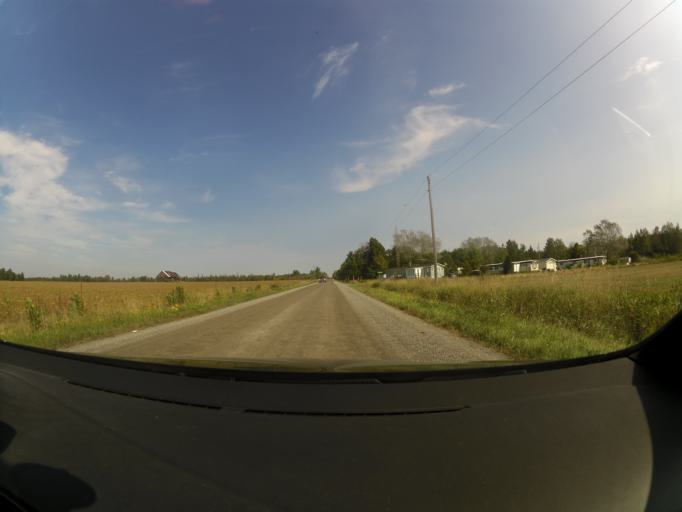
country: CA
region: Ontario
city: Arnprior
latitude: 45.3412
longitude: -76.2107
